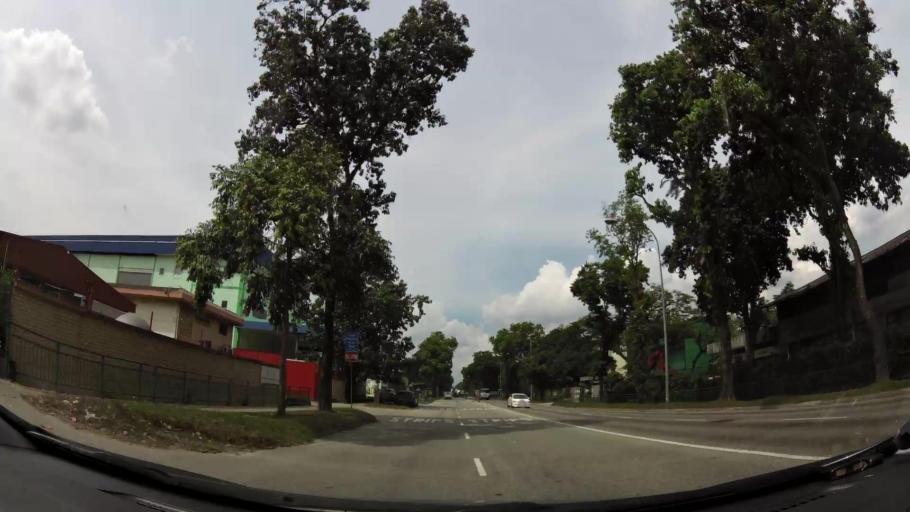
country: MY
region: Johor
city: Johor Bahru
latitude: 1.4157
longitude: 103.7514
